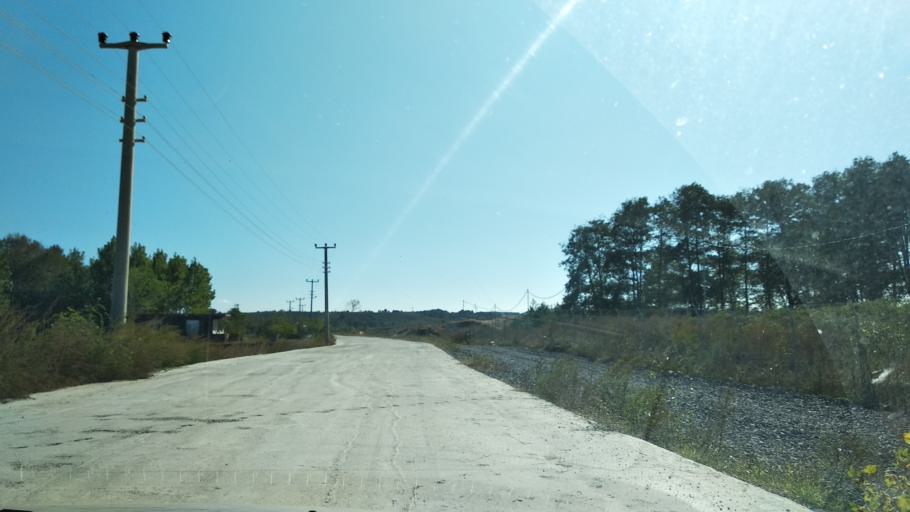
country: TR
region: Sakarya
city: Karasu
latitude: 41.1259
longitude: 30.6086
